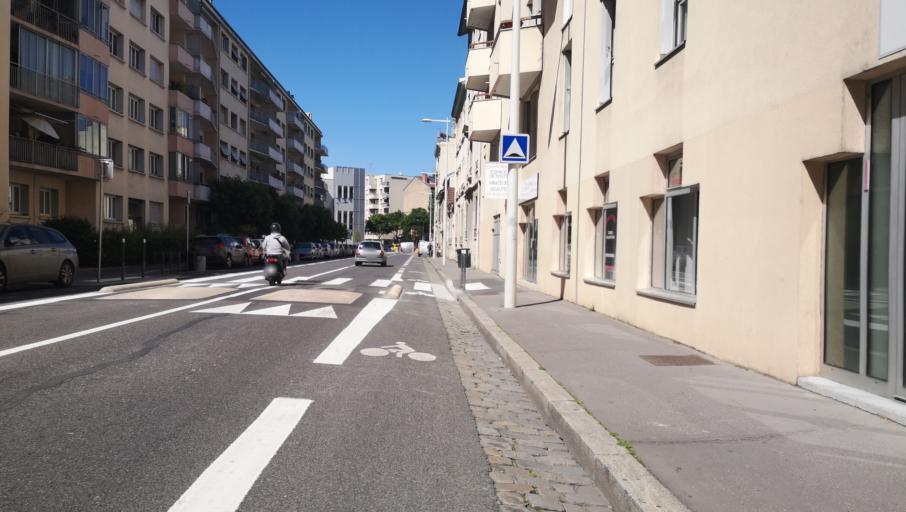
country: FR
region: Rhone-Alpes
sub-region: Departement du Rhone
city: Villeurbanne
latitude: 45.7536
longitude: 4.8770
